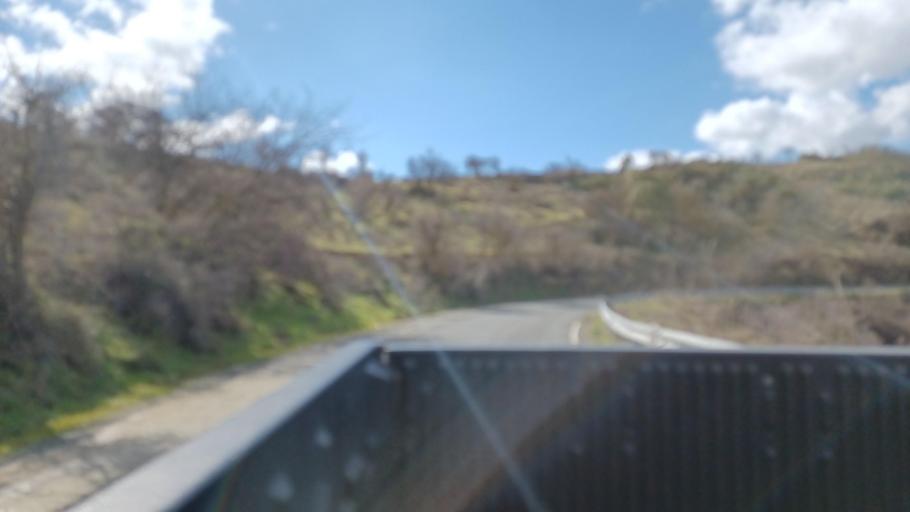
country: CY
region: Limassol
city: Pachna
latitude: 34.8043
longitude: 32.7576
